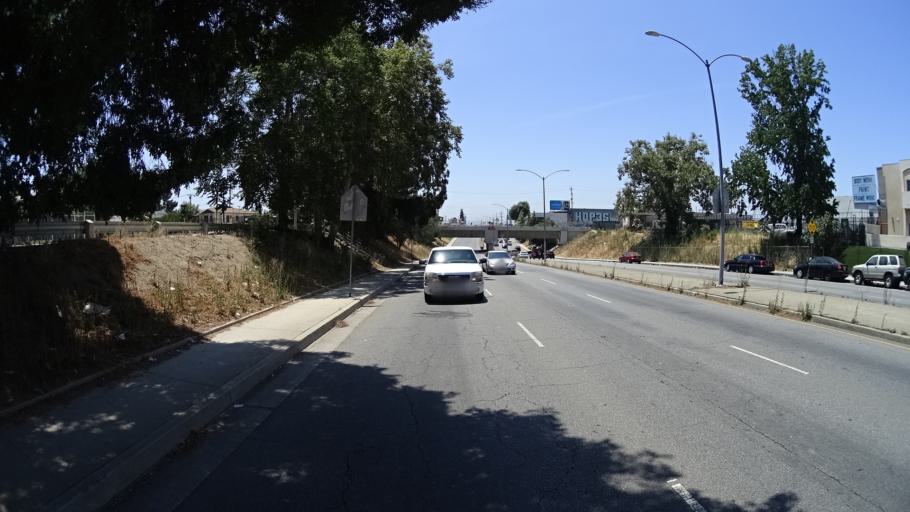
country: US
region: California
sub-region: Los Angeles County
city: Van Nuys
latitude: 34.2164
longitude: -118.4661
